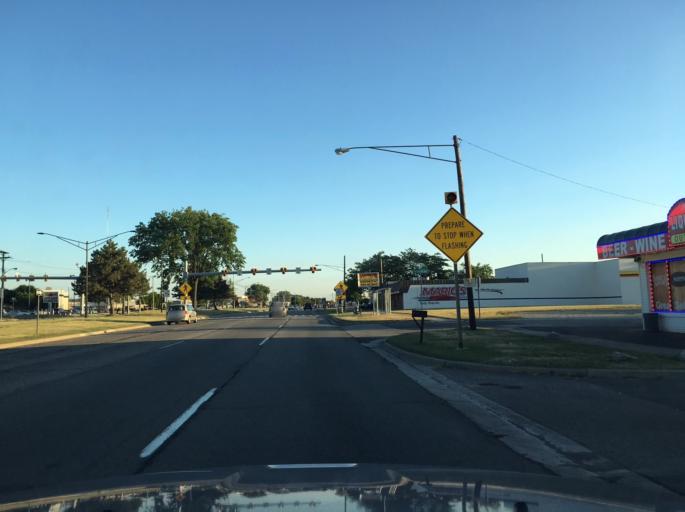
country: US
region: Michigan
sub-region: Macomb County
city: Clinton
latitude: 42.5525
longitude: -82.9011
